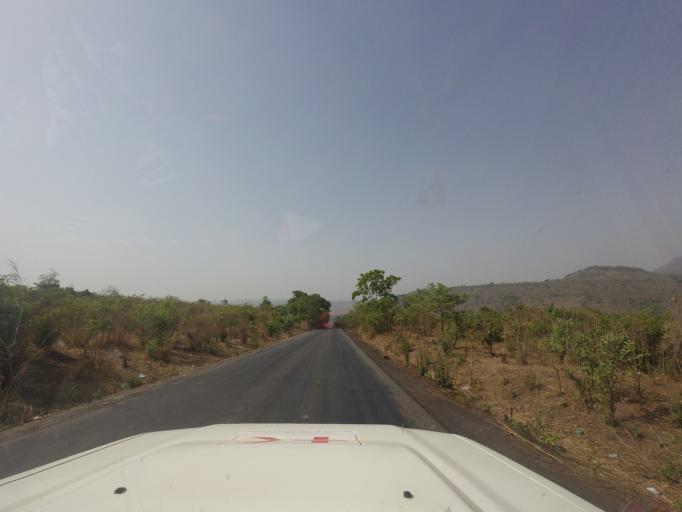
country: GN
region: Mamou
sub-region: Mamou Prefecture
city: Mamou
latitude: 10.2198
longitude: -12.4618
